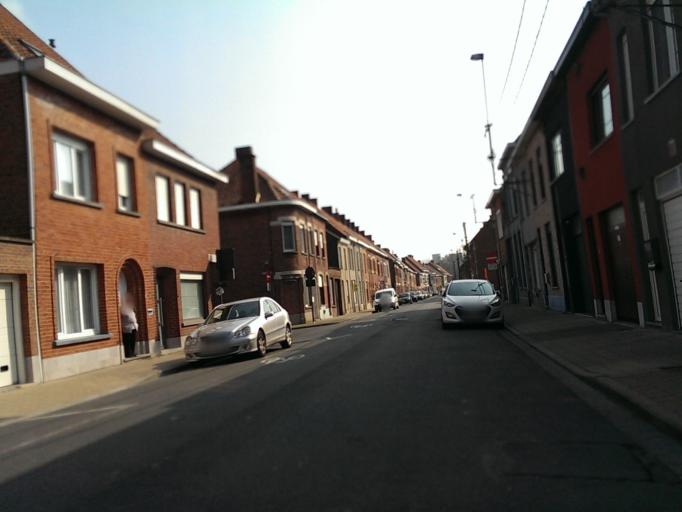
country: BE
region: Flanders
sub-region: Provincie West-Vlaanderen
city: Roeselare
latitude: 50.9484
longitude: 3.1384
